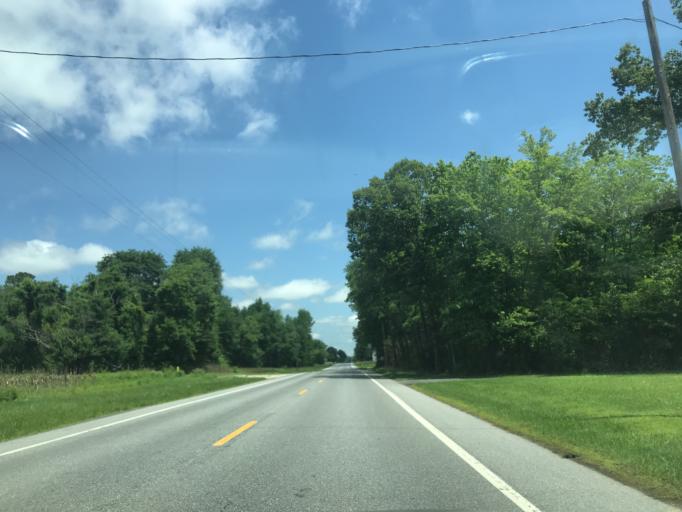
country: US
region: Maryland
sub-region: Caroline County
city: Federalsburg
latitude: 38.7140
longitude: -75.7431
